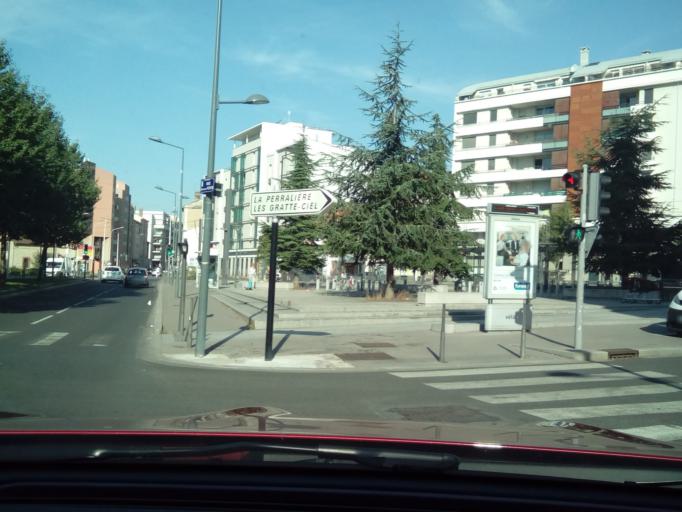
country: FR
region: Rhone-Alpes
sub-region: Departement du Rhone
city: Villeurbanne
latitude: 45.7542
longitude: 4.8859
